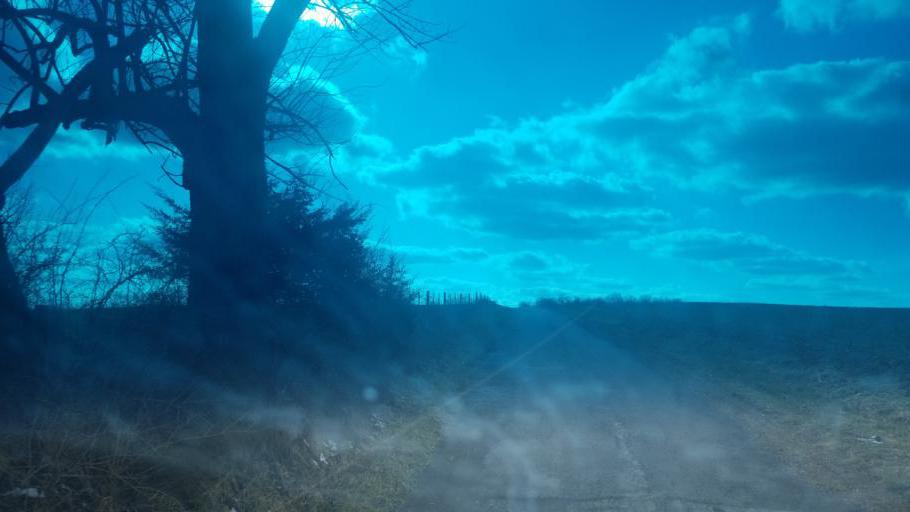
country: US
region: Ohio
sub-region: Highland County
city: Greenfield
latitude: 39.3173
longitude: -83.4117
